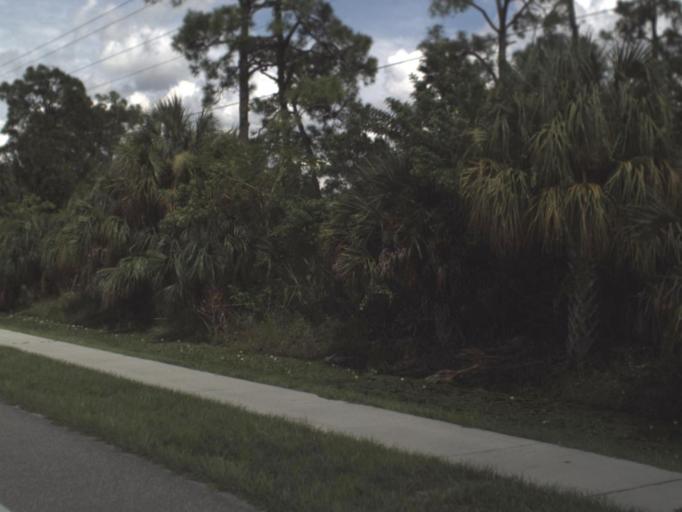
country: US
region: Florida
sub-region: Collier County
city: Immokalee
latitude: 26.5338
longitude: -81.4354
